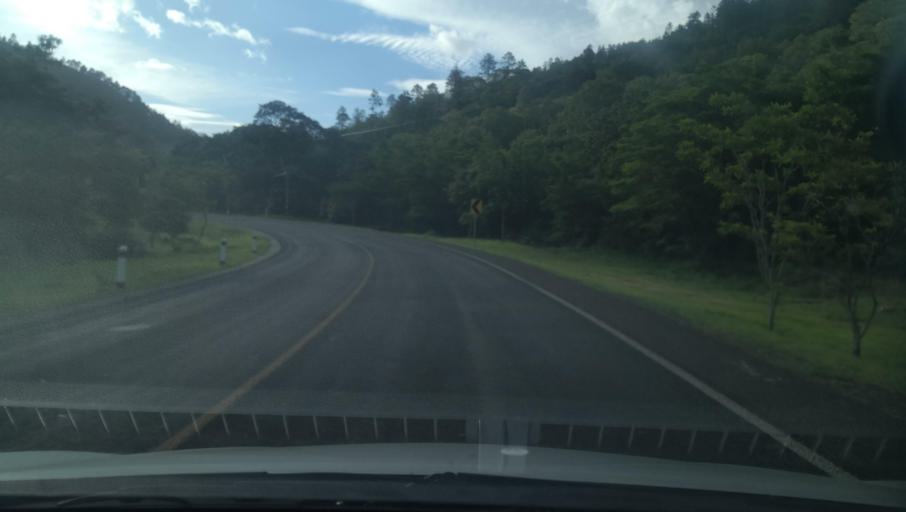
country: NI
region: Nueva Segovia
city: Mozonte
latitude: 13.7013
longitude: -86.4918
